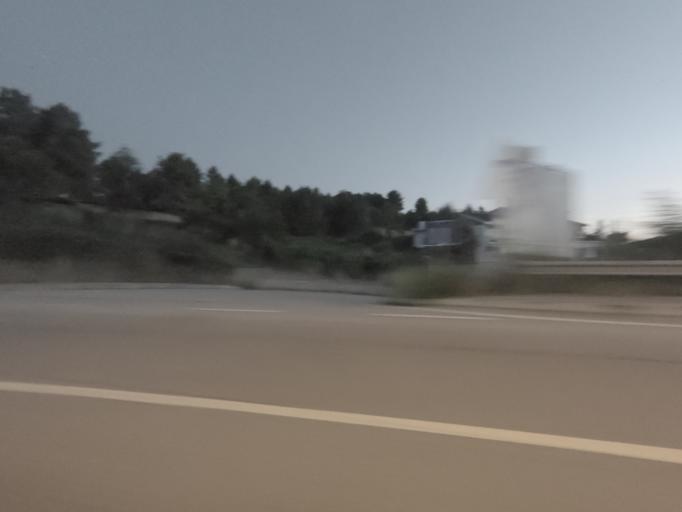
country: PT
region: Vila Real
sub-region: Vila Real
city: Vila Real
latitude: 41.2796
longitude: -7.7209
